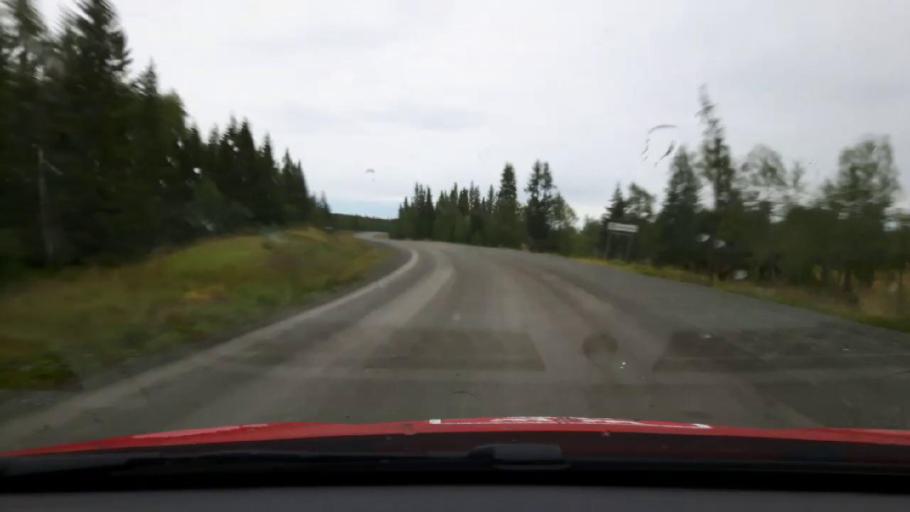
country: SE
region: Jaemtland
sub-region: Are Kommun
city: Are
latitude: 63.4695
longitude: 12.5991
